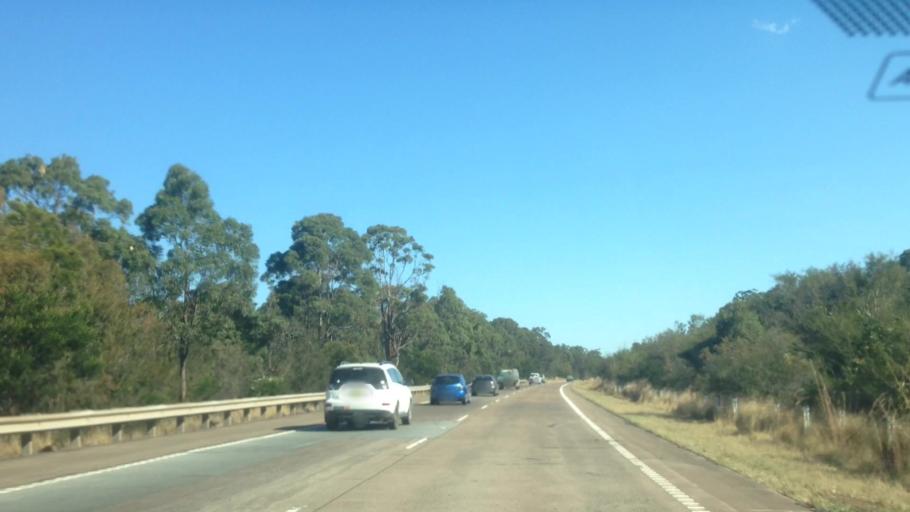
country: AU
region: New South Wales
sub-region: Wyong Shire
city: Charmhaven
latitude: -33.1957
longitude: 151.4654
